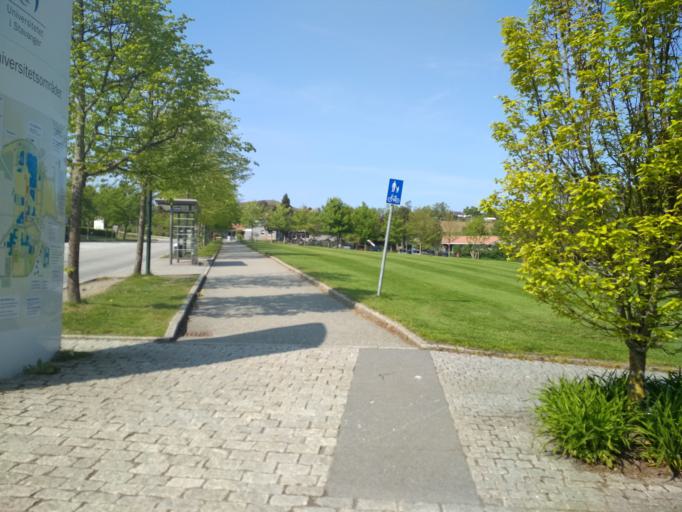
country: NO
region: Rogaland
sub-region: Stavanger
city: Stavanger
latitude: 58.9377
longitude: 5.6982
